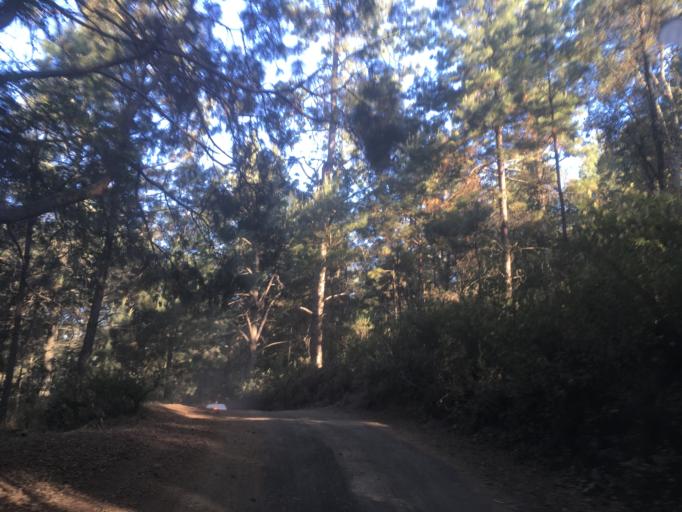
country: MX
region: Michoacan
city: Angahuan
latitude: 19.4780
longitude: -102.2450
